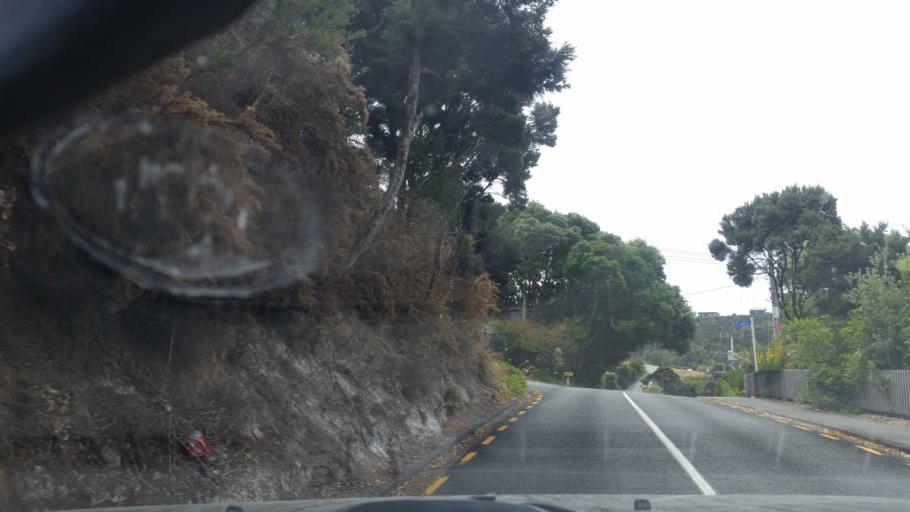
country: NZ
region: Auckland
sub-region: Auckland
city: Wellsford
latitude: -36.0842
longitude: 174.5874
